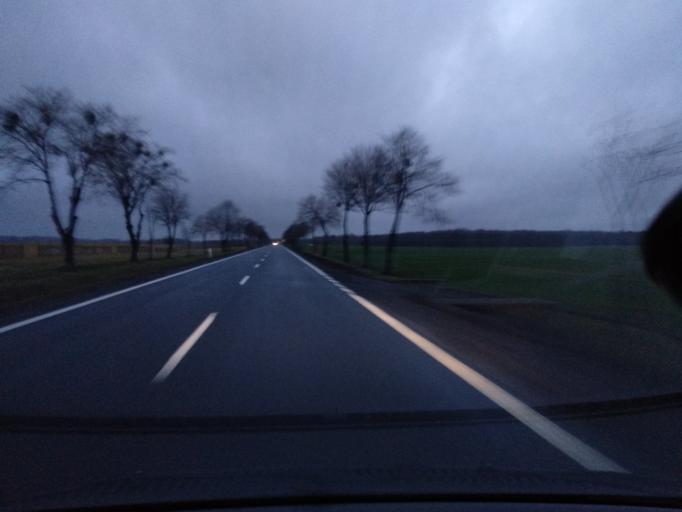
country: PL
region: Lower Silesian Voivodeship
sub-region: Powiat sredzki
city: Ciechow
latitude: 51.1671
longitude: 16.5582
